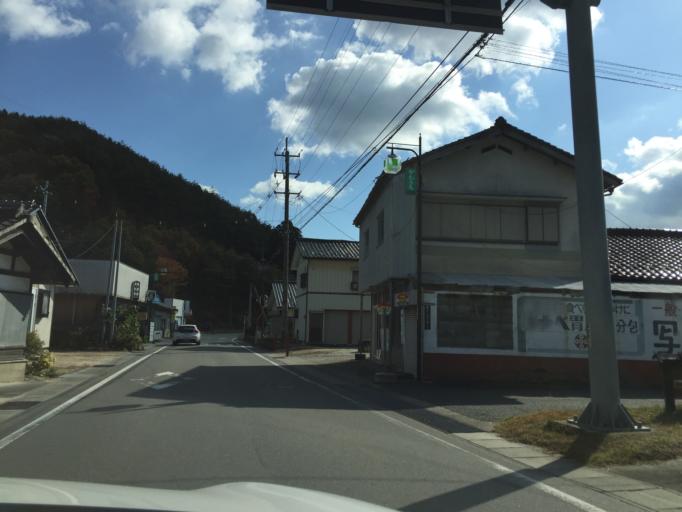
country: JP
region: Fukushima
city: Namie
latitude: 37.3415
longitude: 140.8058
